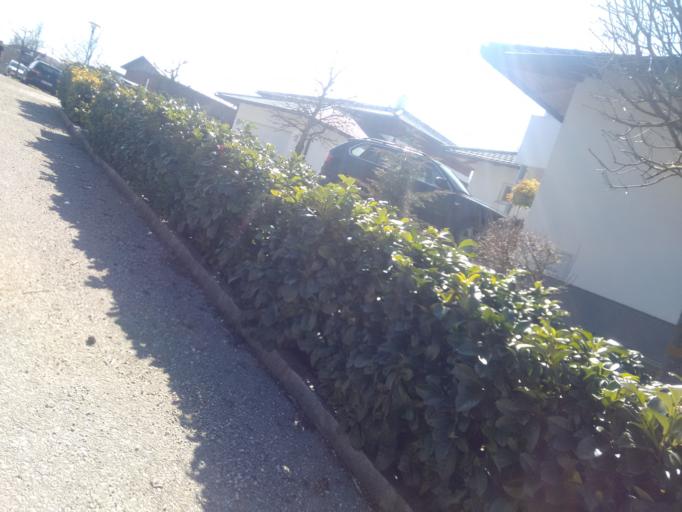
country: AT
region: Upper Austria
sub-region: Politischer Bezirk Grieskirchen
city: Bad Schallerbach
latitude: 48.2077
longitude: 13.9572
